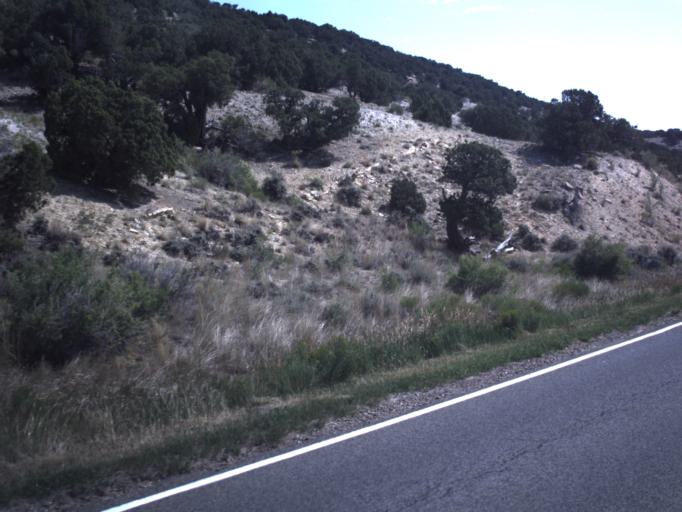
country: US
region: Utah
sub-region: Daggett County
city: Manila
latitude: 40.9784
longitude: -109.7841
